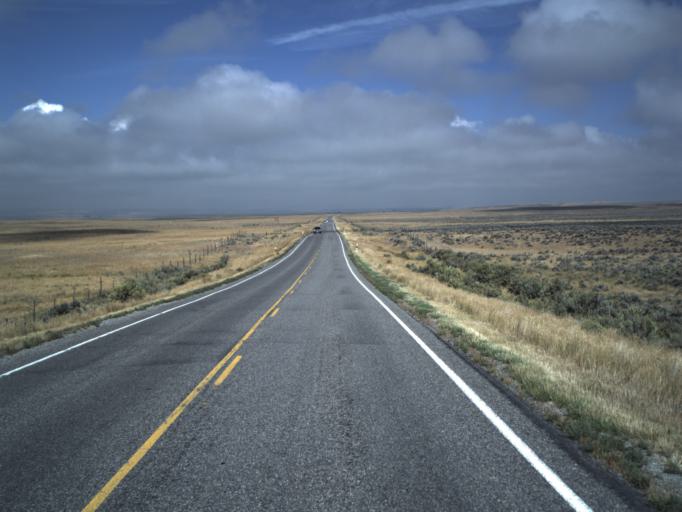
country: US
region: Wyoming
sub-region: Uinta County
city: Evanston
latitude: 41.4488
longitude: -111.0838
